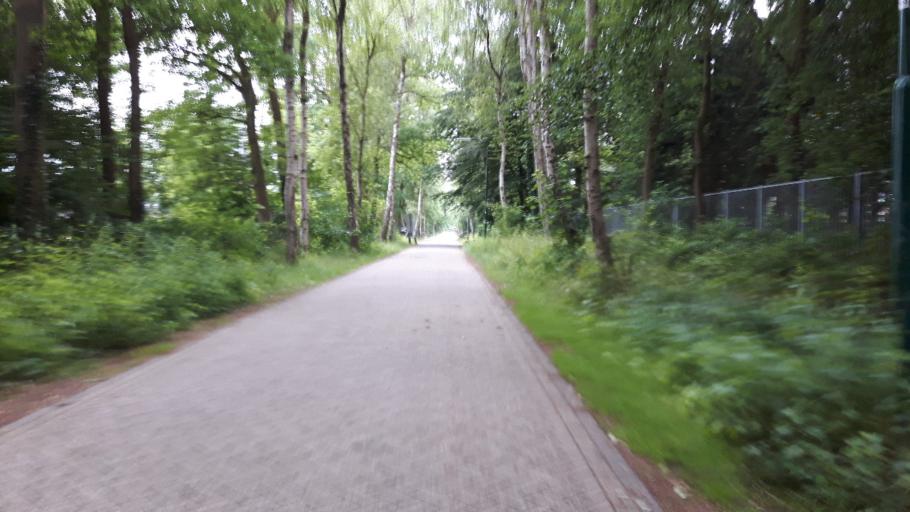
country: NL
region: Utrecht
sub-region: Gemeente De Bilt
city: De Bilt
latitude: 52.1369
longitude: 5.1983
